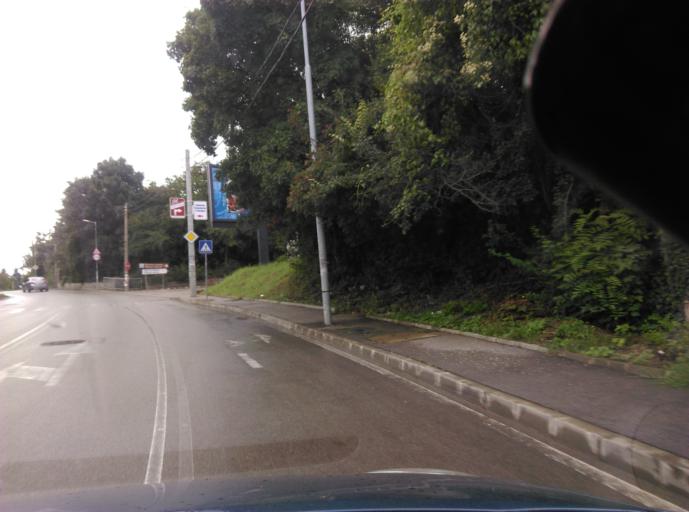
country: BG
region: Sofia-Capital
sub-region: Stolichna Obshtina
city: Sofia
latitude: 42.6458
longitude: 23.2737
